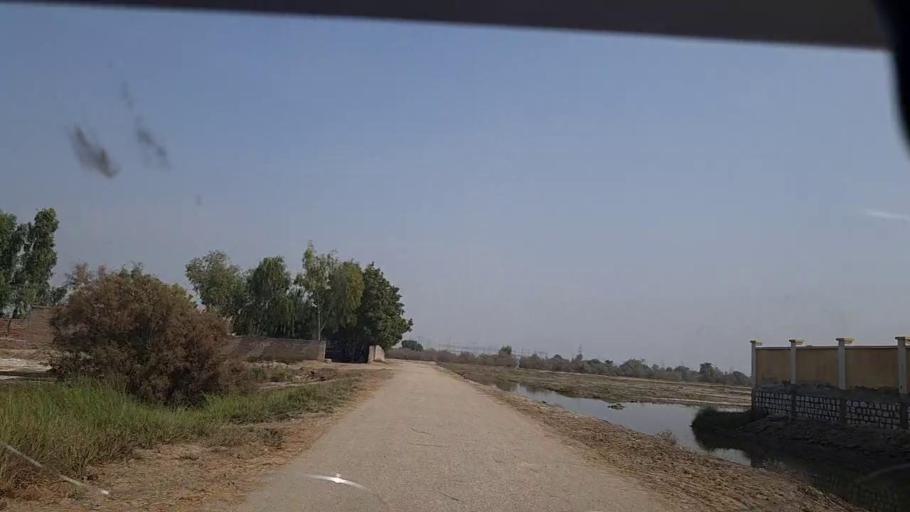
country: PK
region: Sindh
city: Shikarpur
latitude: 28.0269
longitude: 68.6183
